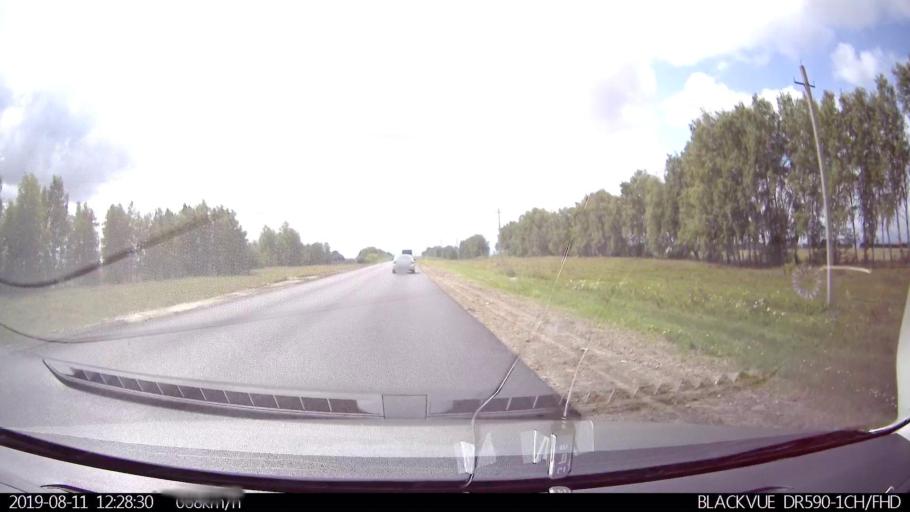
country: RU
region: Ulyanovsk
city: Ignatovka
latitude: 53.8438
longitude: 47.9113
